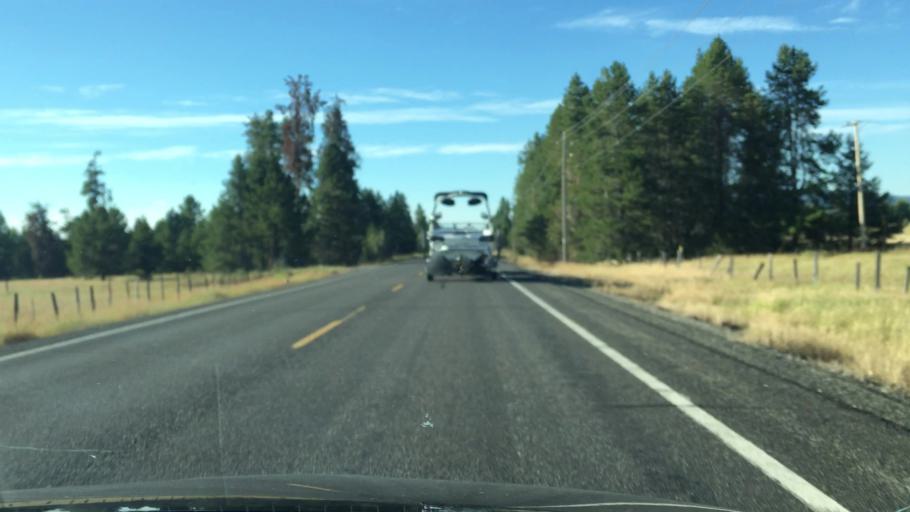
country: US
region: Idaho
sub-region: Valley County
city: Cascade
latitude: 44.4534
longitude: -115.9993
